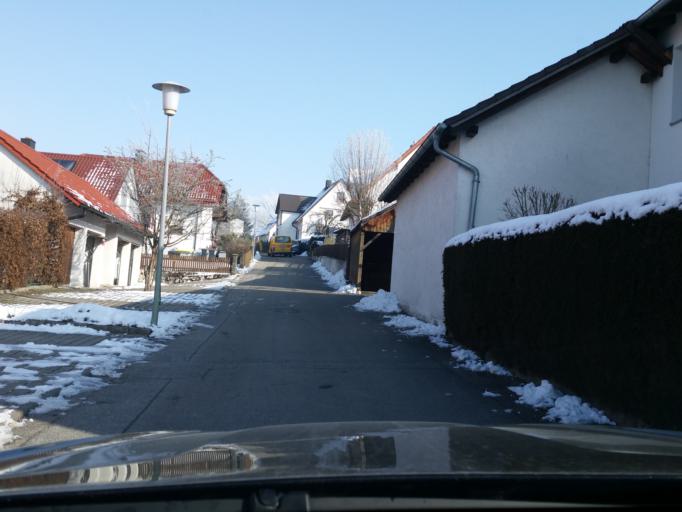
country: DE
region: Bavaria
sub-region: Lower Bavaria
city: Eching
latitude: 48.4993
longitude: 12.0646
